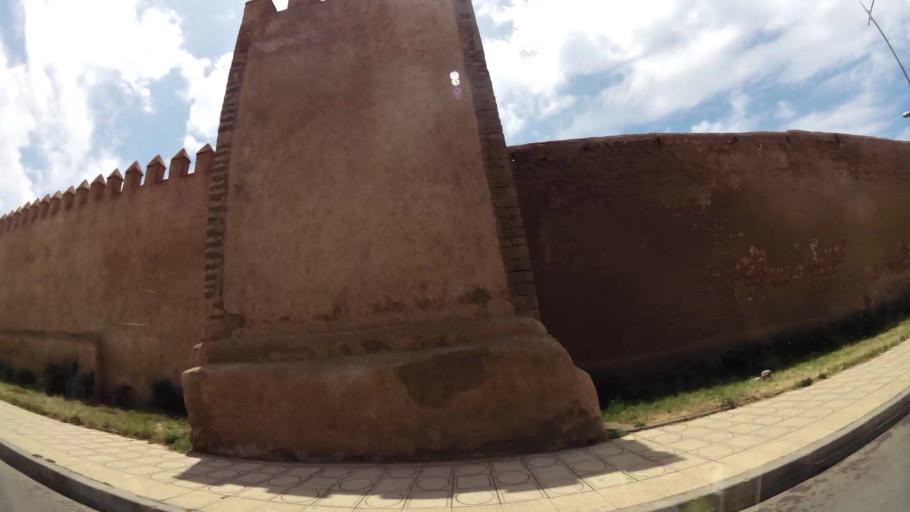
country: MA
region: Rabat-Sale-Zemmour-Zaer
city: Sale
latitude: 34.0452
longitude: -6.8264
